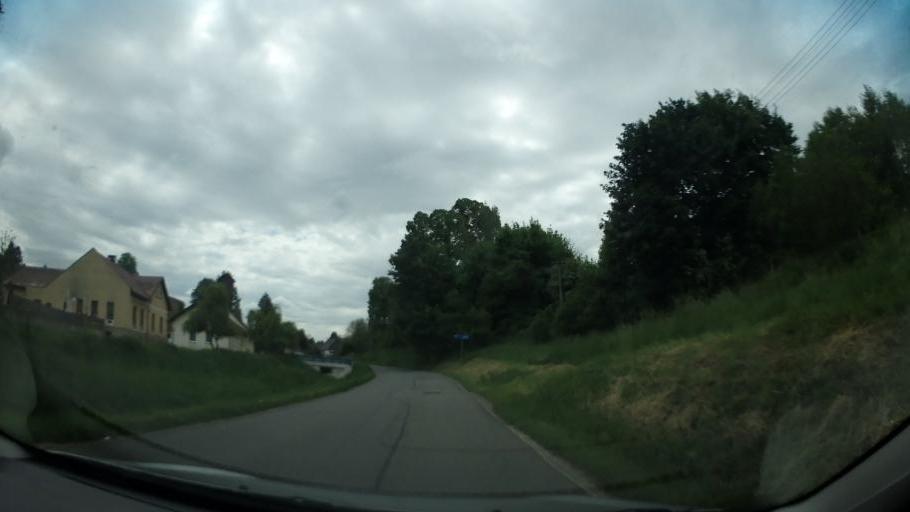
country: CZ
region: Pardubicky
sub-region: Okres Svitavy
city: Moravska Trebova
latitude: 49.8305
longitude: 16.7017
